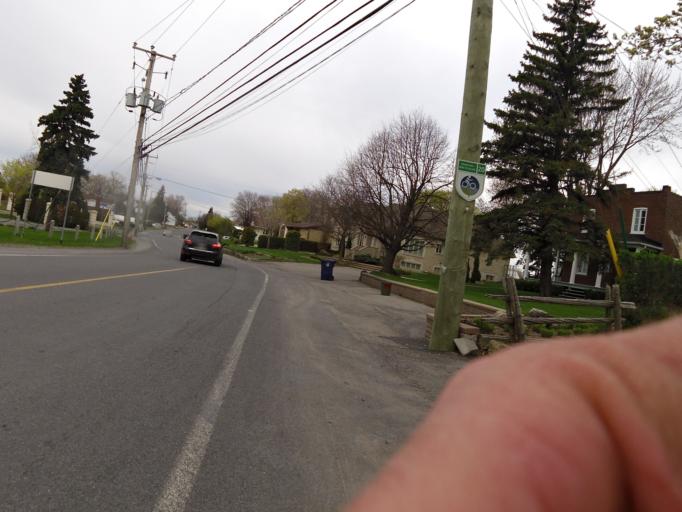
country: CA
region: Quebec
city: Dollard-Des Ormeaux
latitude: 45.5208
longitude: -73.7807
